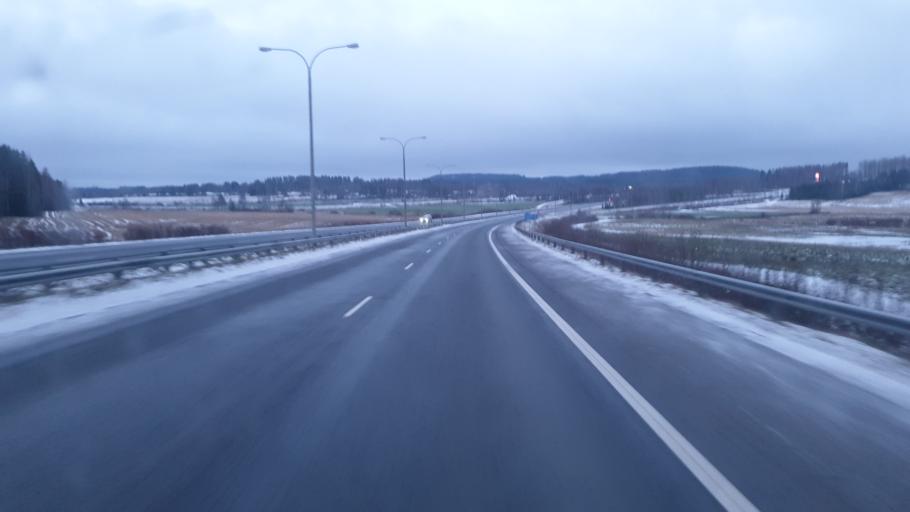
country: FI
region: Northern Savo
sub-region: Kuopio
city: Siilinjaervi
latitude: 62.9960
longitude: 27.6977
